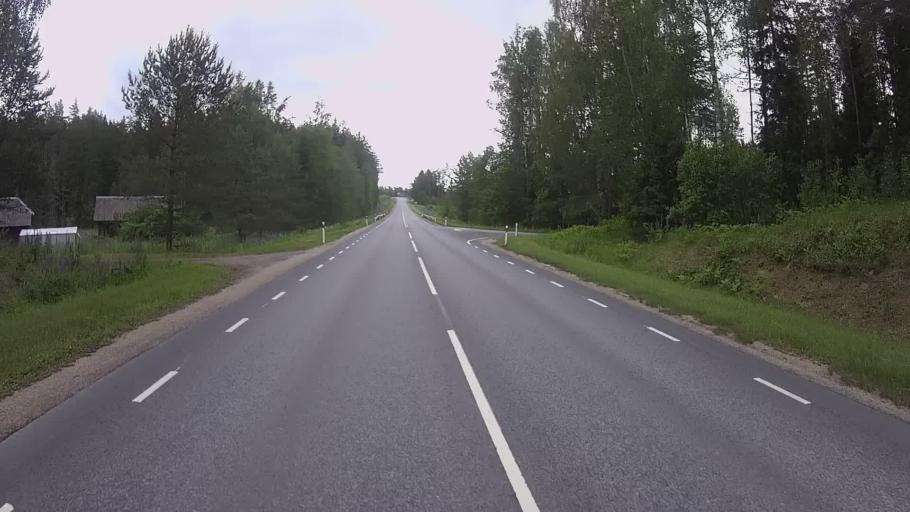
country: EE
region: Polvamaa
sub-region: Polva linn
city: Polva
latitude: 58.0995
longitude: 26.9985
